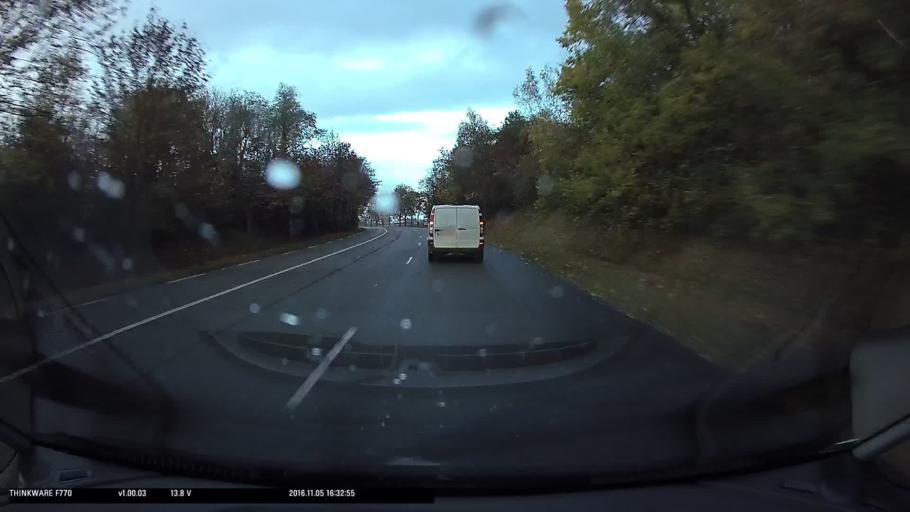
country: FR
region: Ile-de-France
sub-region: Departement du Val-d'Oise
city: Sagy
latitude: 49.0585
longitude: 1.9630
